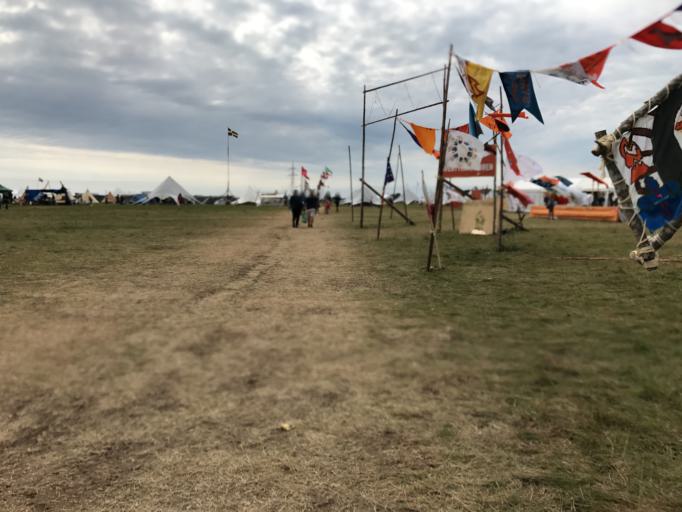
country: SE
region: Skane
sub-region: Kristianstads Kommun
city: Fjalkinge
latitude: 56.0040
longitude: 14.2987
